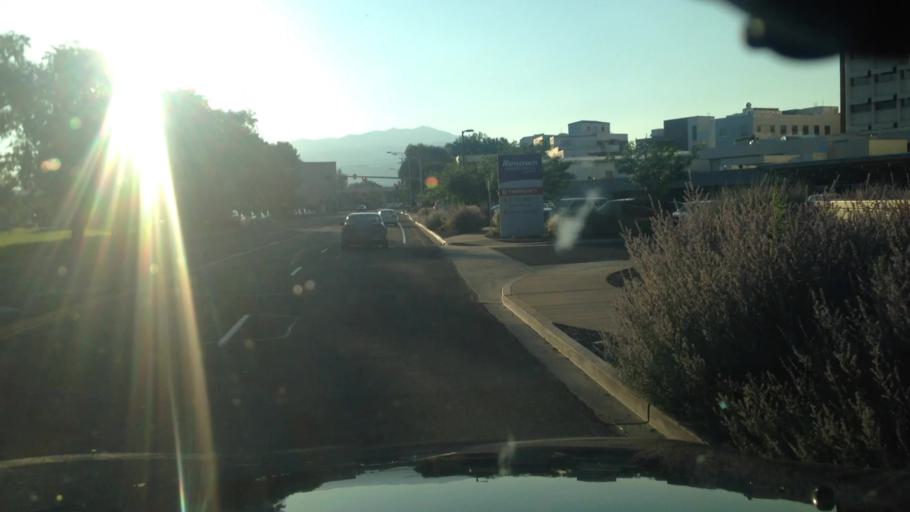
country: US
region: Nevada
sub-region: Washoe County
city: Reno
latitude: 39.5243
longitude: -119.7957
